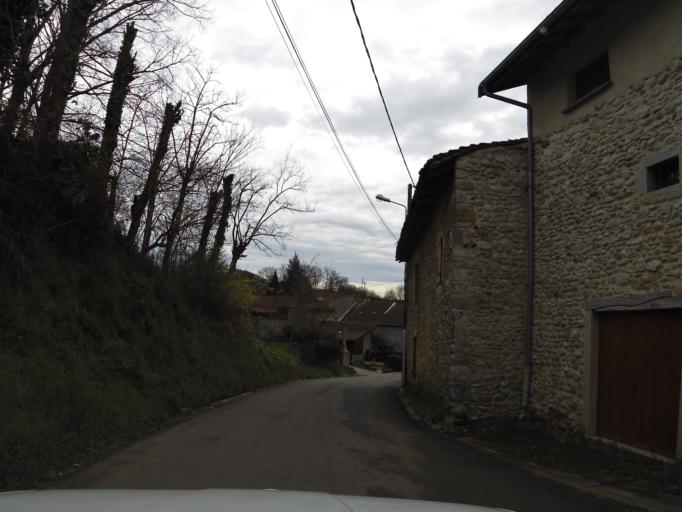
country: FR
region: Rhone-Alpes
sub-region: Departement de l'Ain
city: Lagnieu
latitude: 45.8865
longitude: 5.3138
